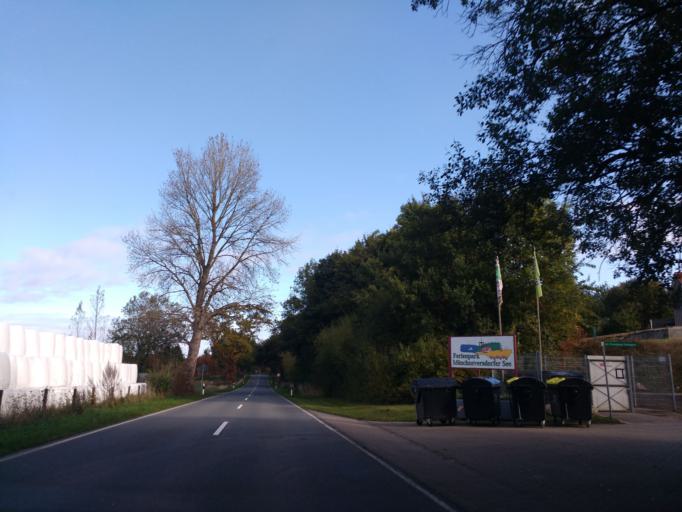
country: DE
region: Schleswig-Holstein
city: Schonwalde am Bungsberg
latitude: 54.2211
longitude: 10.7386
